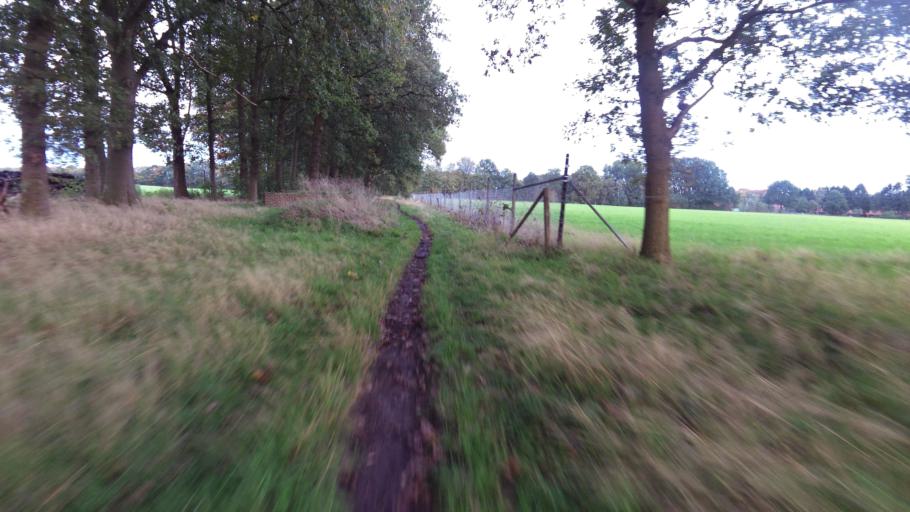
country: NL
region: Gelderland
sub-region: Gemeente Renkum
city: Wolfheze
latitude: 52.0127
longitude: 5.7934
